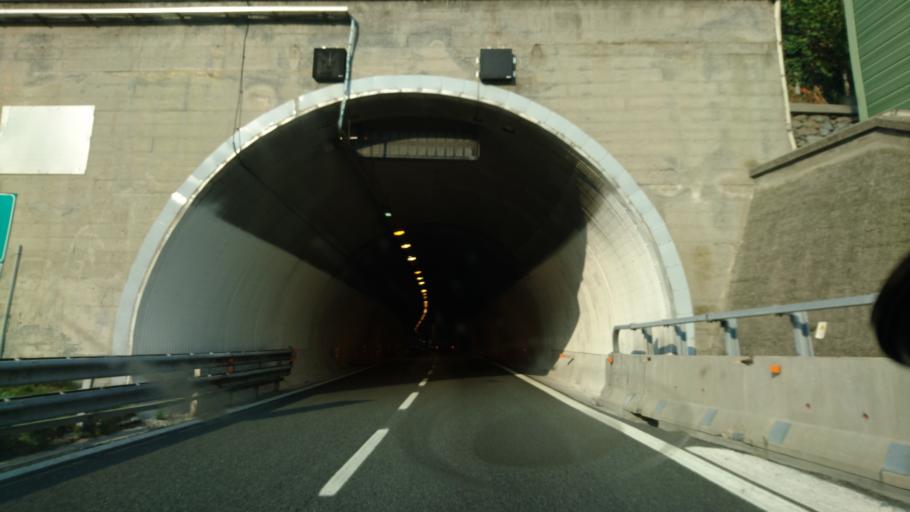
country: IT
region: Liguria
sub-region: Provincia di Savona
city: Albisola Marina
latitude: 44.3312
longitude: 8.4994
